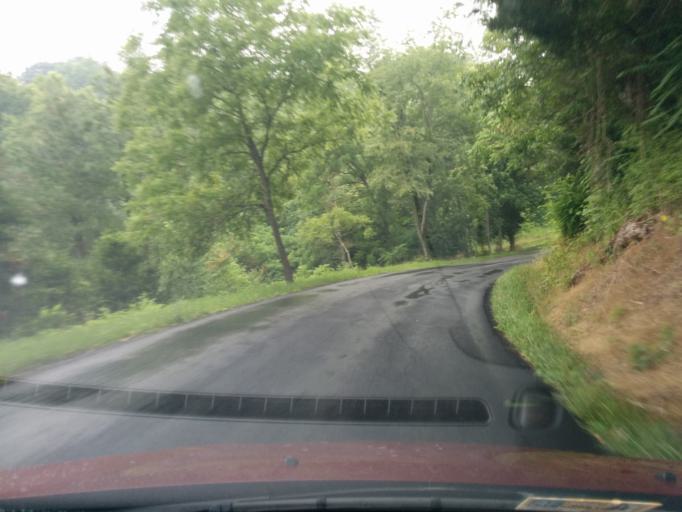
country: US
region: Virginia
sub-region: Rockbridge County
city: East Lexington
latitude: 37.8564
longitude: -79.4247
